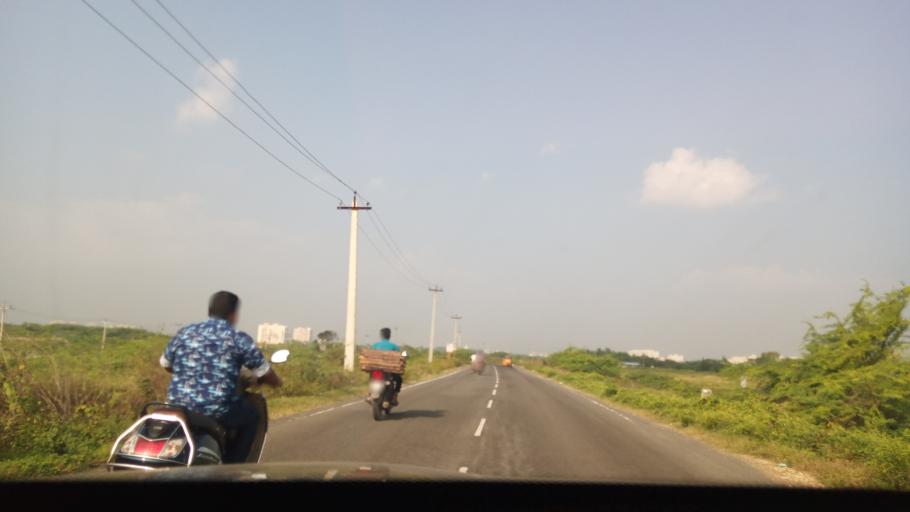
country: IN
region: Tamil Nadu
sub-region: Kancheepuram
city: Injambakkam
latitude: 12.7840
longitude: 80.2431
